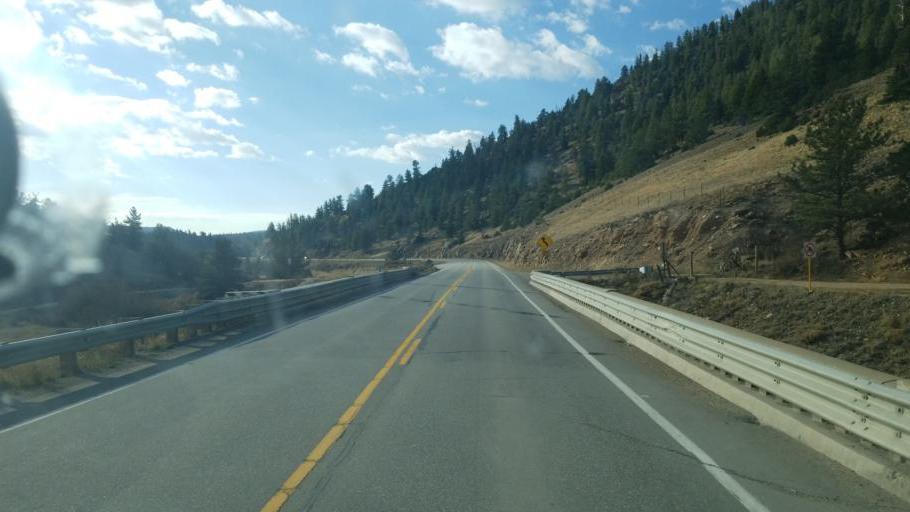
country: US
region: Colorado
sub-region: Chaffee County
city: Buena Vista
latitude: 38.8587
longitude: -105.9862
